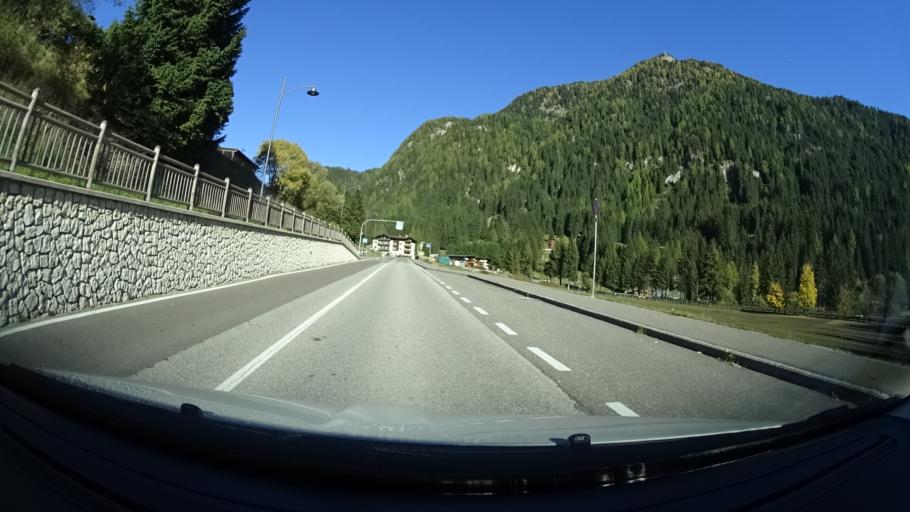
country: IT
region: Trentino-Alto Adige
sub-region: Provincia di Trento
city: Pozza di Fassa
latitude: 46.4393
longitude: 11.6939
